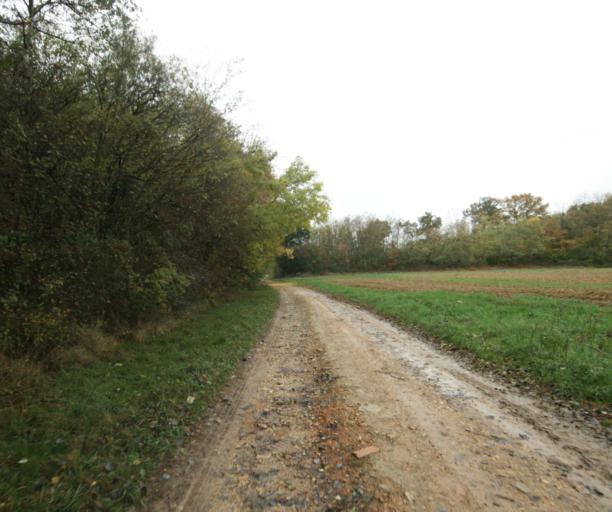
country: FR
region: Bourgogne
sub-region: Departement de Saone-et-Loire
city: Saint-Martin-Belle-Roche
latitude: 46.4785
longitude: 4.8495
